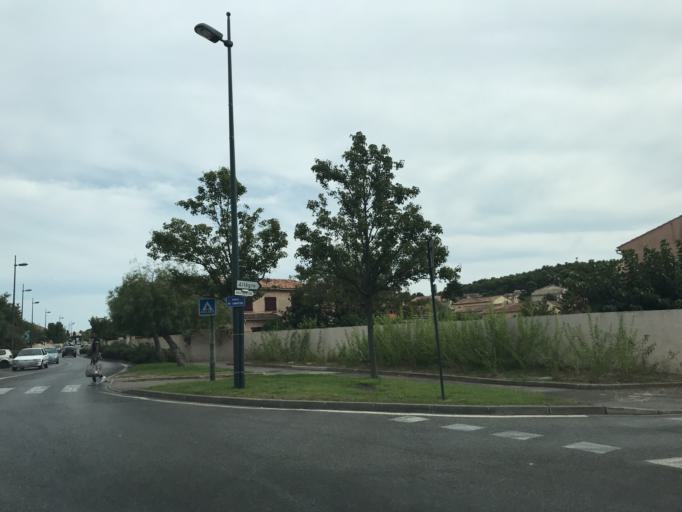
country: FR
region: Provence-Alpes-Cote d'Azur
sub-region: Departement du Var
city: Six-Fours-les-Plages
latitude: 43.0907
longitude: 5.8491
